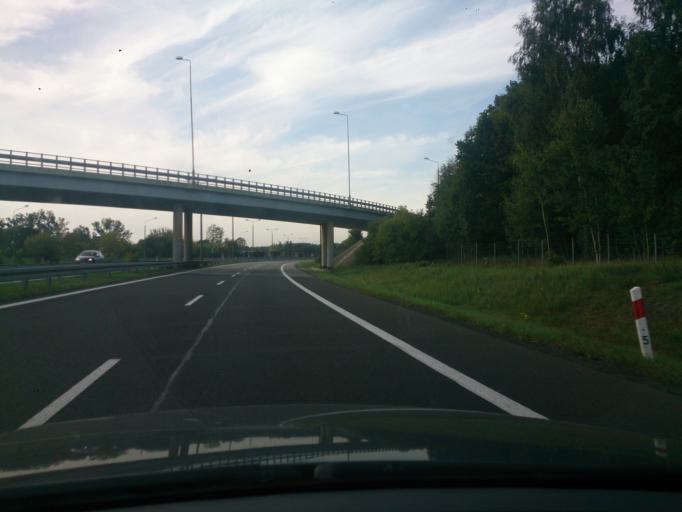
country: PL
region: Kujawsko-Pomorskie
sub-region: Powiat chelminski
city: Chelmno
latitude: 53.3803
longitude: 18.3466
